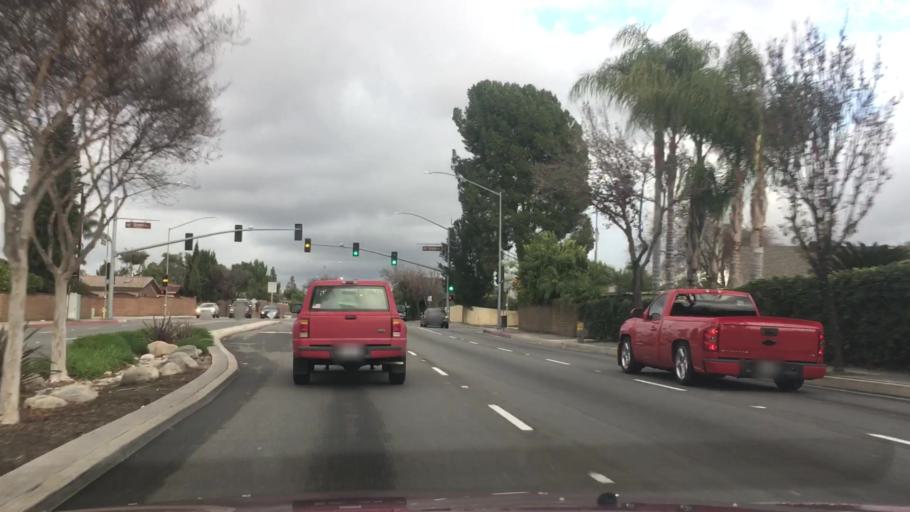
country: US
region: California
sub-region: Los Angeles County
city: La Mirada
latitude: 33.9164
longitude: -118.0039
